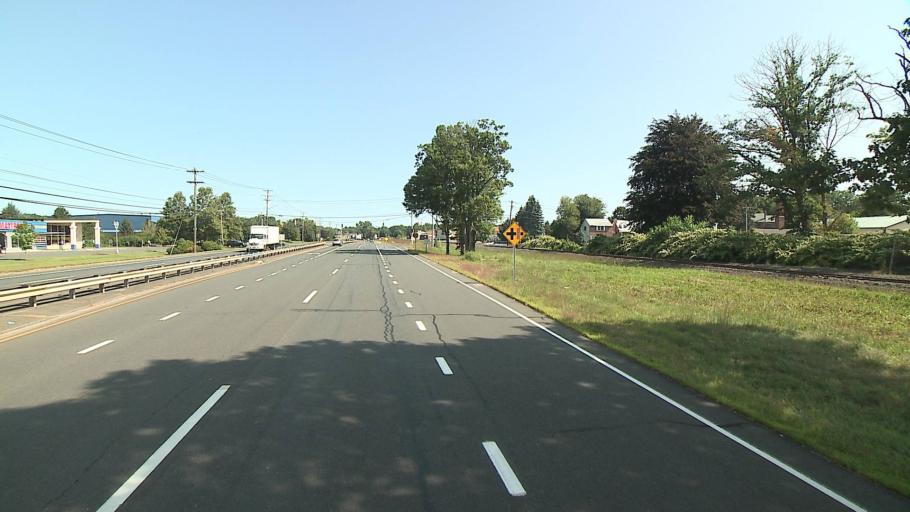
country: US
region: Connecticut
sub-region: Hartford County
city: South Windsor
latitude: 41.8411
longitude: -72.6012
